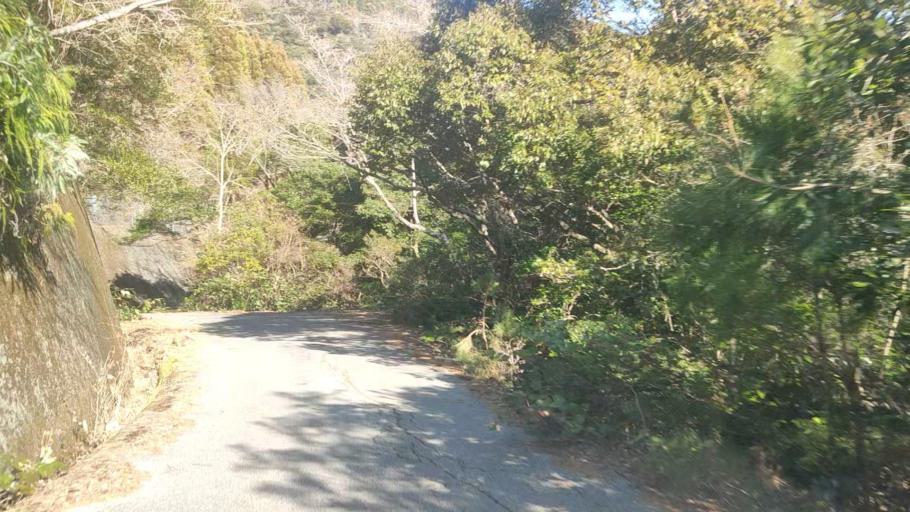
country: JP
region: Oita
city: Saiki
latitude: 32.7839
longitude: 131.8517
